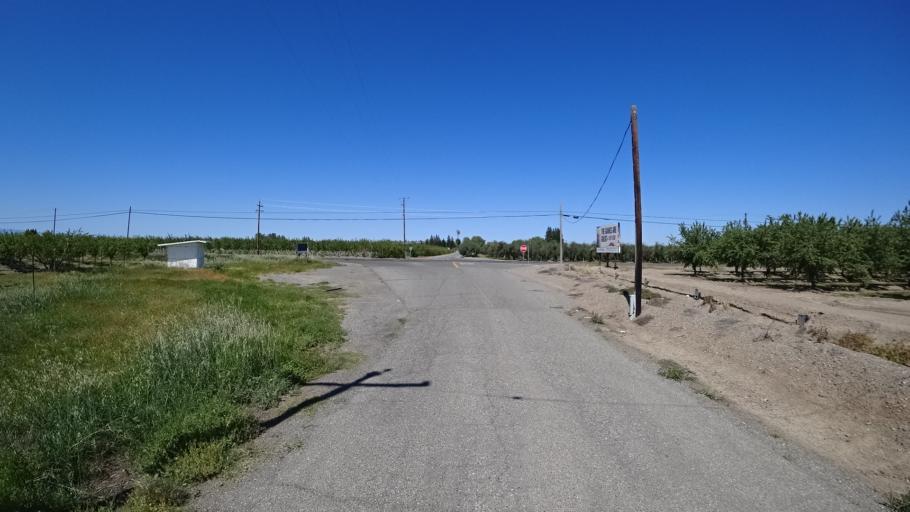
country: US
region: California
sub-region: Glenn County
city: Orland
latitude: 39.7465
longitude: -122.1503
